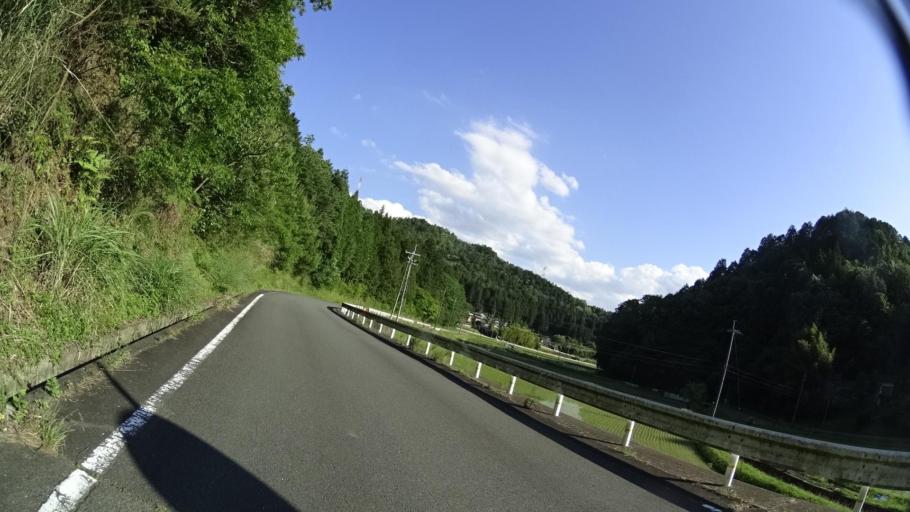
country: JP
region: Kyoto
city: Kameoka
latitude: 34.9684
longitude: 135.5625
